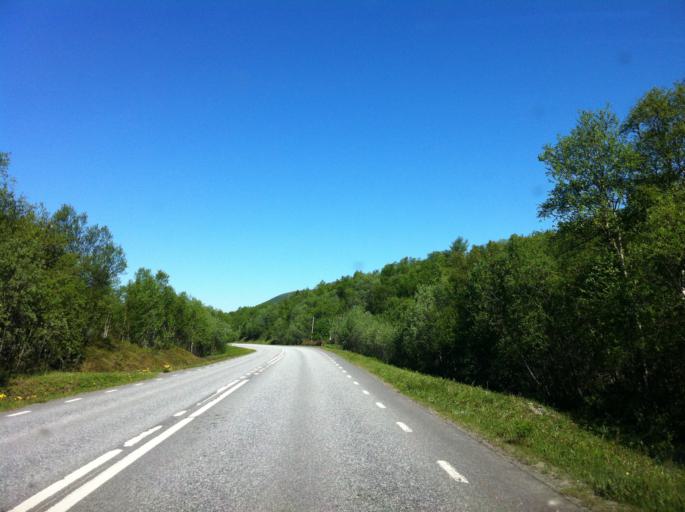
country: NO
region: Hedmark
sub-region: Engerdal
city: Engerdal
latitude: 62.5354
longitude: 12.3608
